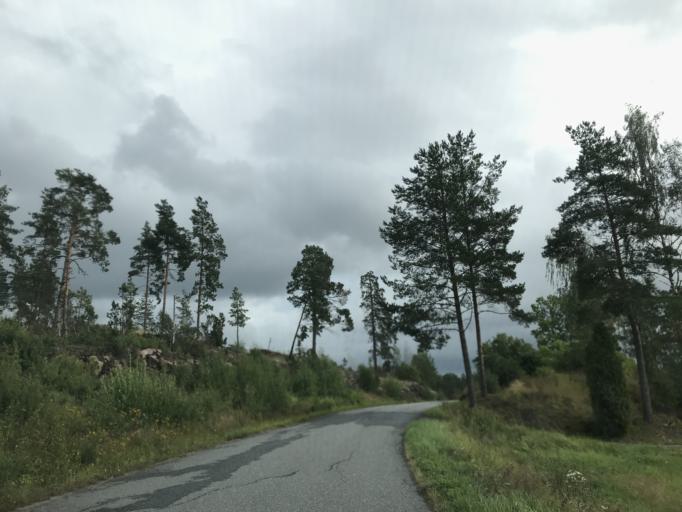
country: FI
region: Varsinais-Suomi
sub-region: Salo
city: Pernioe
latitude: 60.0754
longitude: 23.1292
